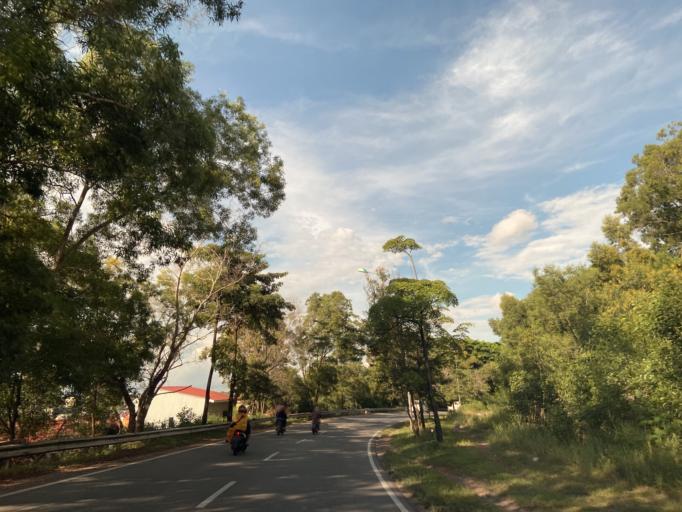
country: SG
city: Singapore
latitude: 1.1232
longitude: 104.0094
